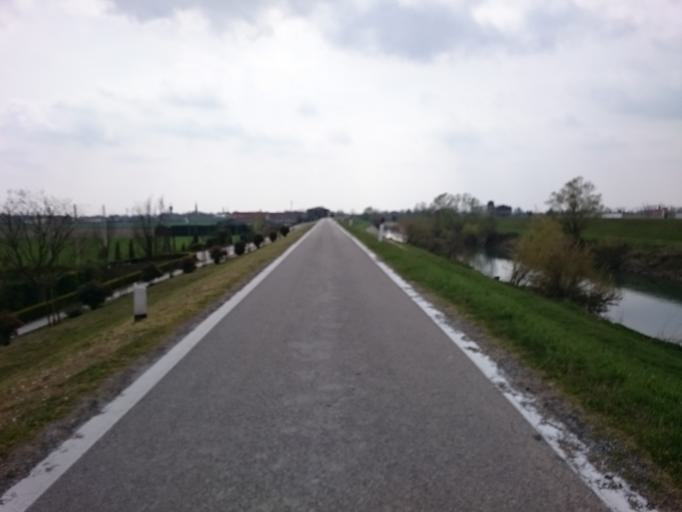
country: IT
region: Veneto
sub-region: Provincia di Padova
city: Bovolenta
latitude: 45.2803
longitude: 11.9336
